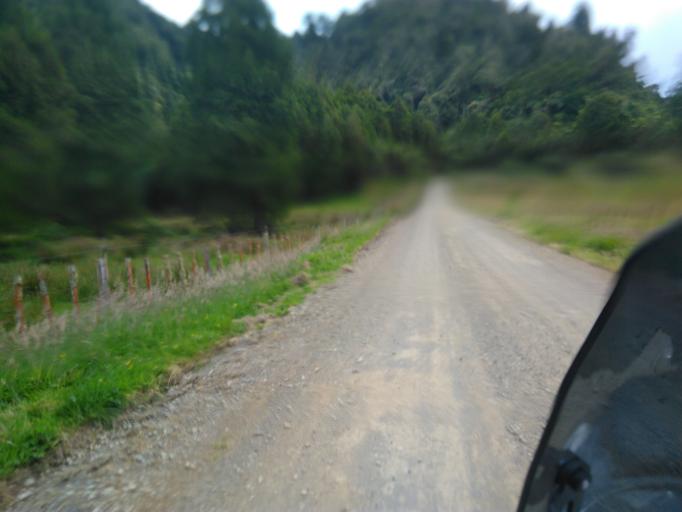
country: NZ
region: Bay of Plenty
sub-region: Opotiki District
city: Opotiki
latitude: -38.0992
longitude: 177.4854
